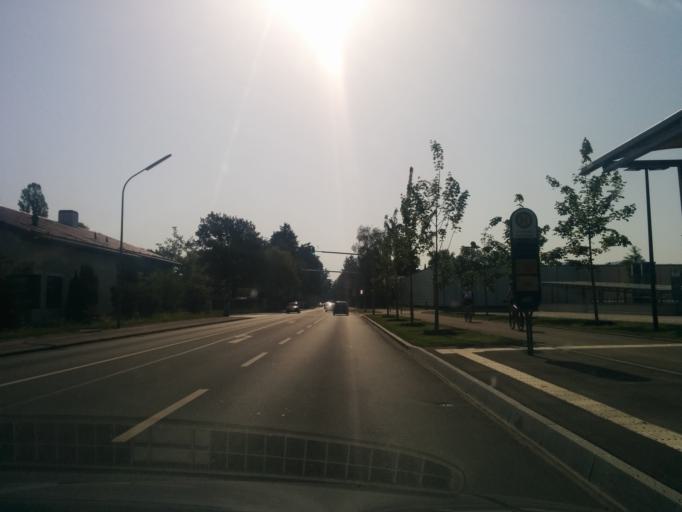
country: DE
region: Bavaria
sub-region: Upper Bavaria
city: Grunwald
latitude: 48.0384
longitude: 11.5268
